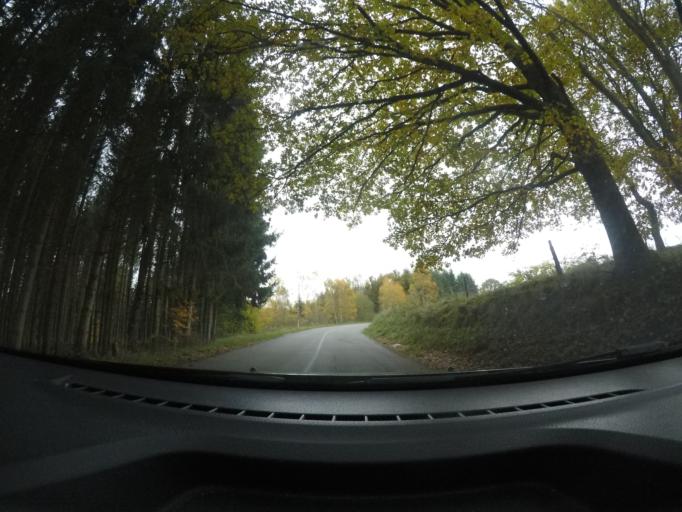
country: BE
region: Wallonia
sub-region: Province du Luxembourg
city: Bertogne
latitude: 50.1273
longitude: 5.7183
